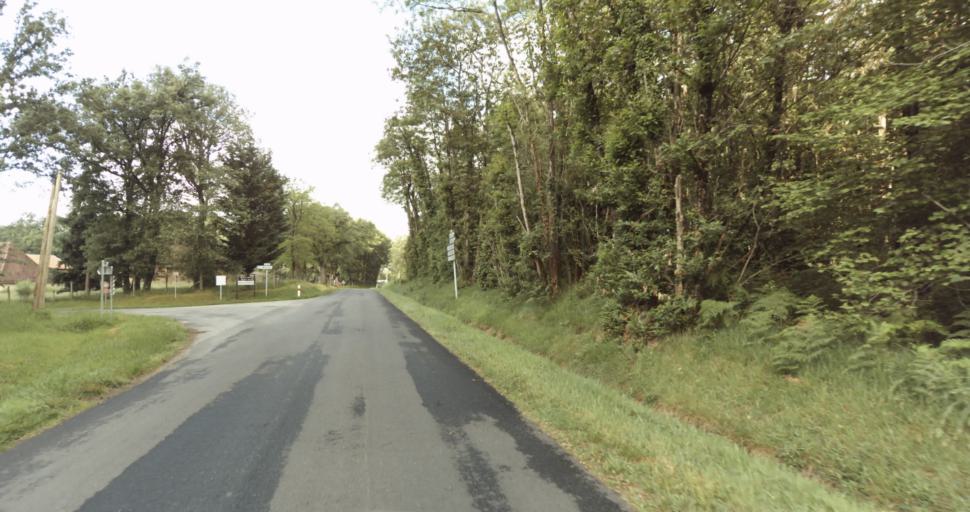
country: FR
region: Aquitaine
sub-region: Departement de la Dordogne
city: Lalinde
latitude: 44.9046
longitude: 0.7783
